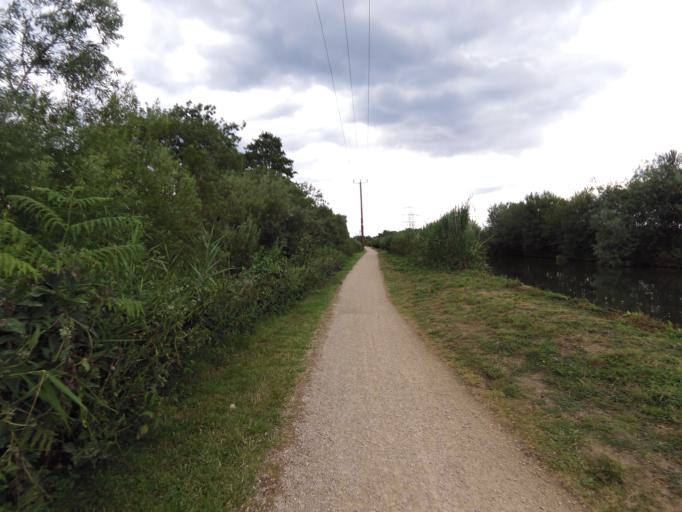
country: GB
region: England
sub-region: Hertfordshire
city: Cheshunt
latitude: 51.7161
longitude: -0.0154
